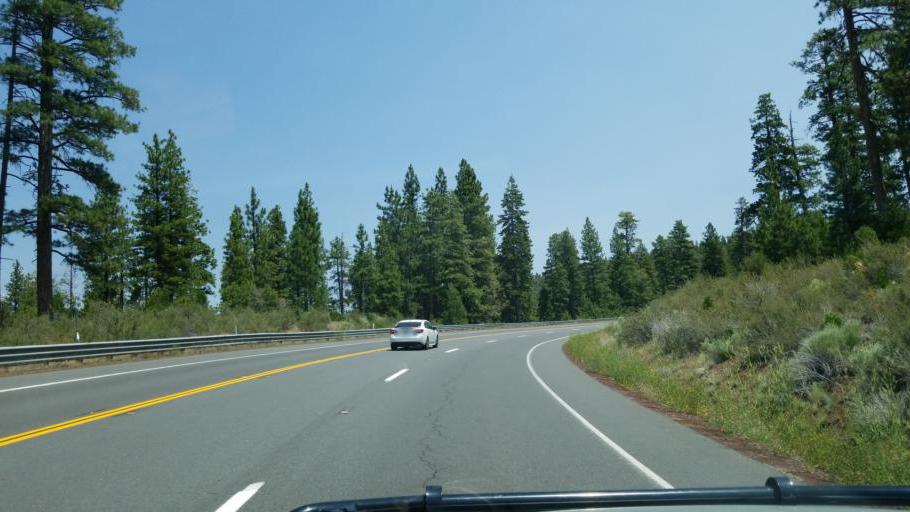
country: US
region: California
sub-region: Shasta County
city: Burney
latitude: 40.7025
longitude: -121.3995
